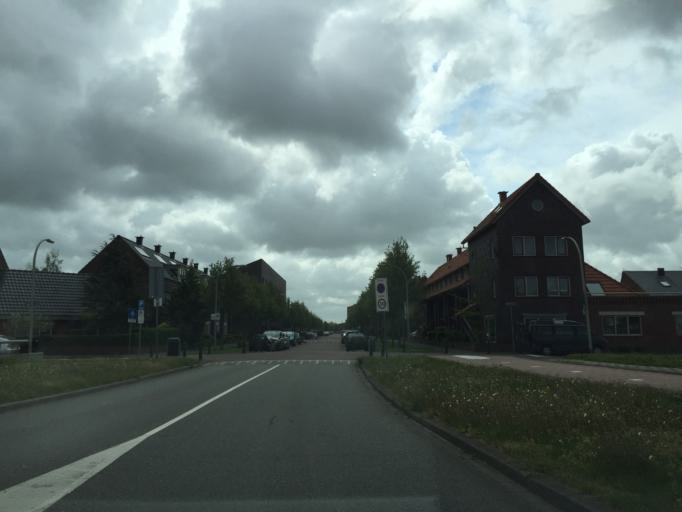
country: NL
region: South Holland
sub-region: Gemeente Den Haag
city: Ypenburg
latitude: 52.0407
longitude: 4.3614
